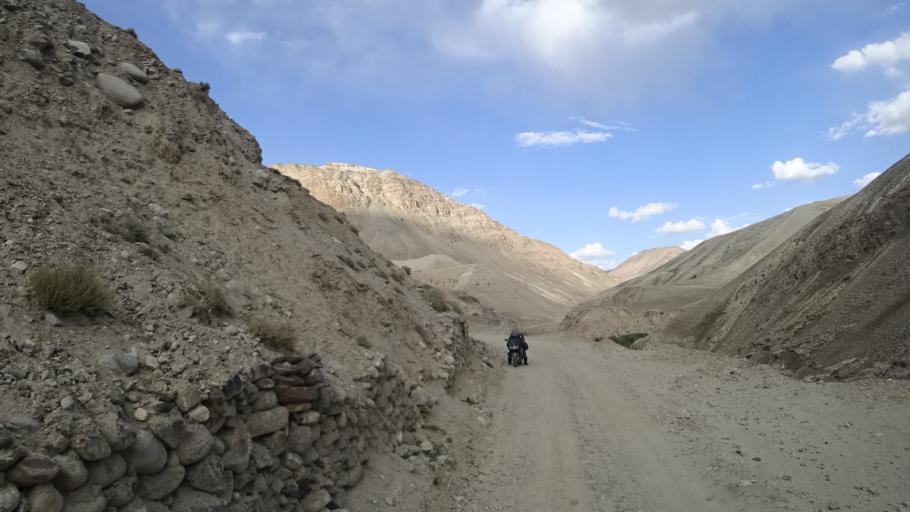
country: AF
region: Badakhshan
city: Khandud
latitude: 37.2331
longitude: 72.8159
